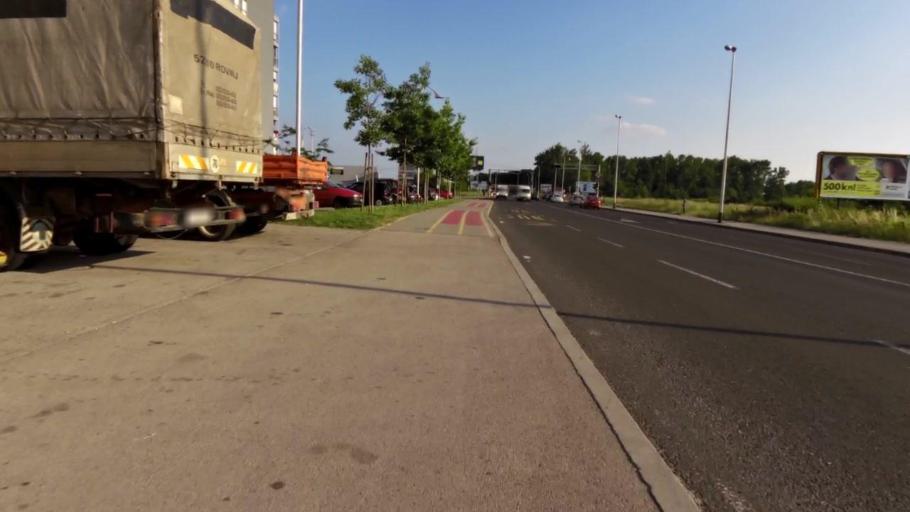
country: HR
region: Grad Zagreb
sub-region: Sesvete
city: Sesvete
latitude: 45.8107
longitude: 16.1014
